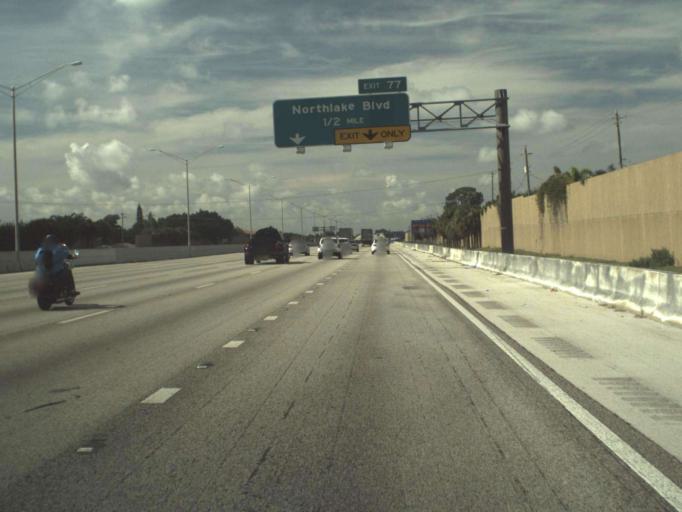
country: US
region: Florida
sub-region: Palm Beach County
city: North Palm Beach
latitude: 26.8195
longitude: -80.0981
